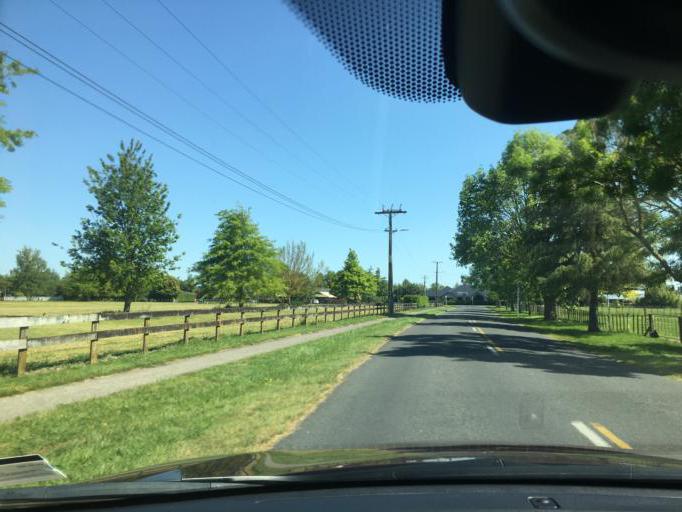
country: NZ
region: Waikato
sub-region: Waipa District
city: Cambridge
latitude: -37.9175
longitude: 175.4702
